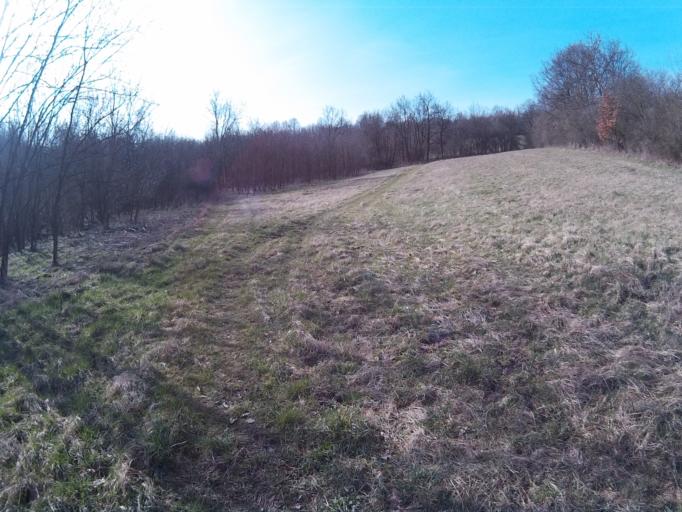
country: HU
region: Nograd
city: Retsag
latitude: 47.8824
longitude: 19.1879
